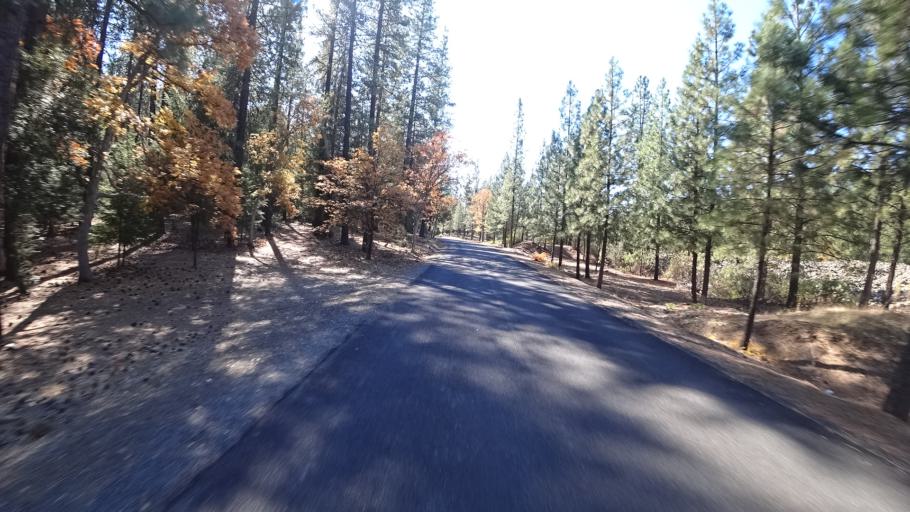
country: US
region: California
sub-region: Siskiyou County
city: Yreka
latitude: 41.6614
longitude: -122.8522
